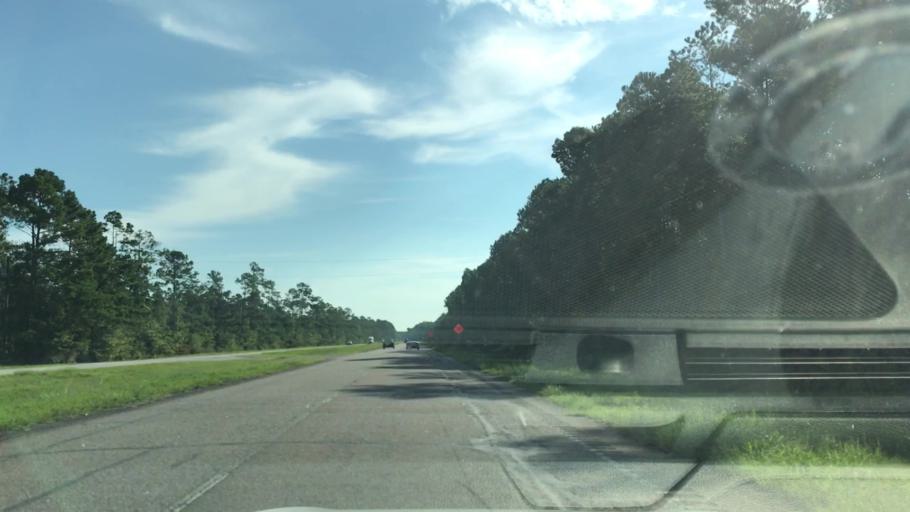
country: US
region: South Carolina
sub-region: Charleston County
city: Awendaw
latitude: 33.0829
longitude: -79.4972
